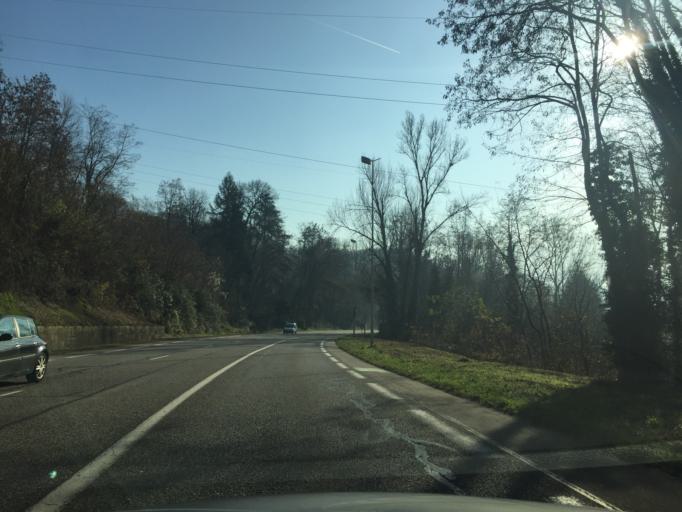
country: FR
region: Rhone-Alpes
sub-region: Departement de la Savoie
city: Cognin
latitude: 45.5914
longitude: 5.9066
